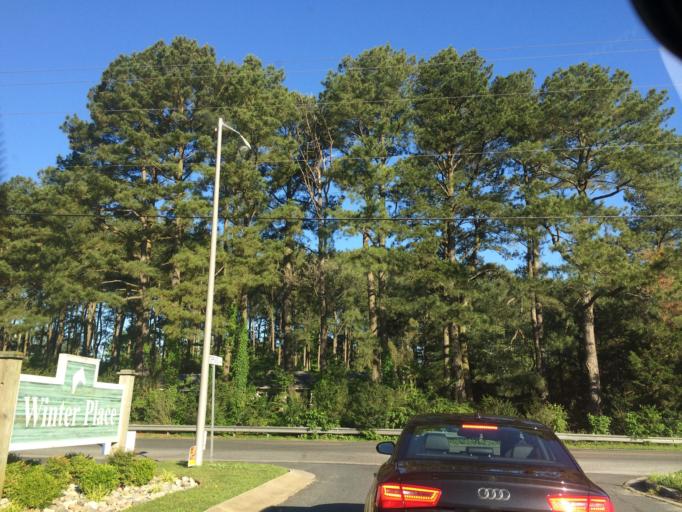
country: US
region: Maryland
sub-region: Wicomico County
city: Salisbury
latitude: 38.3741
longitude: -75.5260
